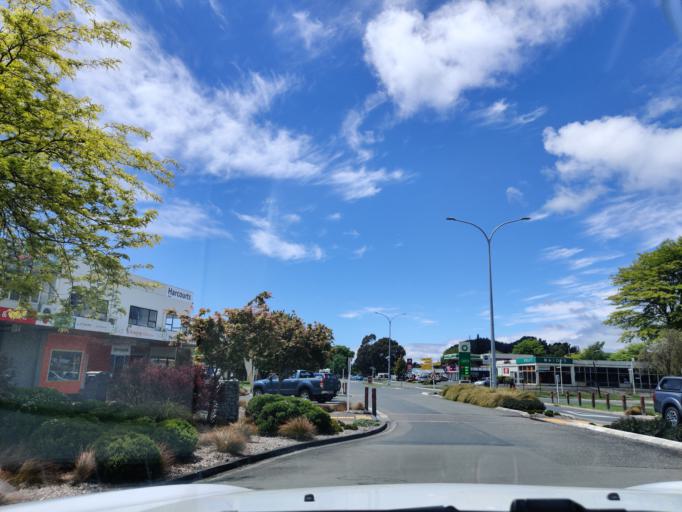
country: NZ
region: Waikato
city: Turangi
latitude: -38.9893
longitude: 175.8096
